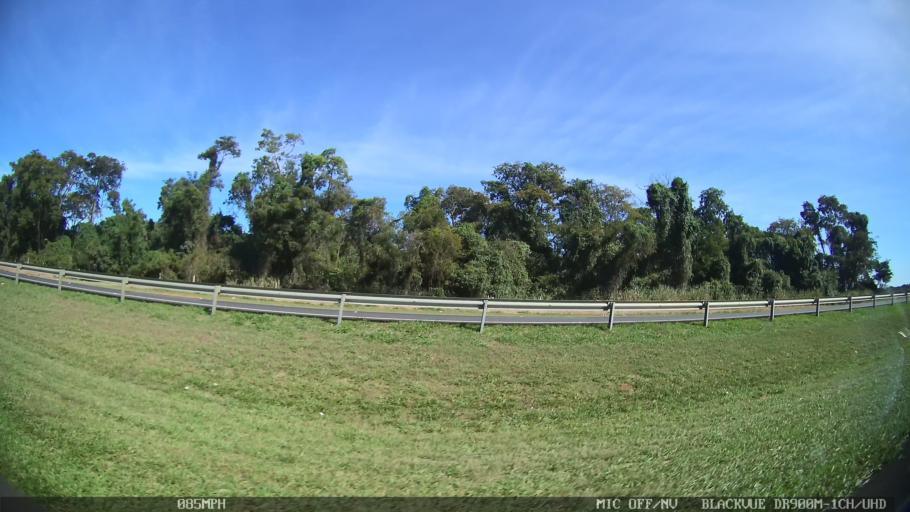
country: BR
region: Sao Paulo
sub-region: Pirassununga
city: Pirassununga
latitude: -21.9359
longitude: -47.4671
